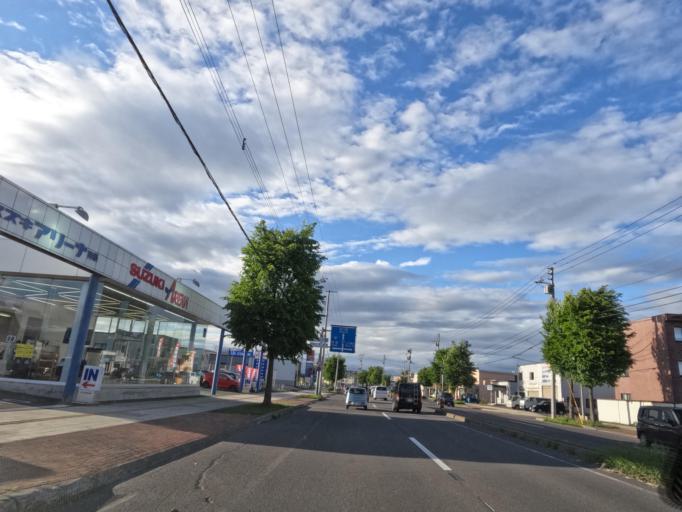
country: JP
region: Hokkaido
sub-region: Asahikawa-shi
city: Asahikawa
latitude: 43.7463
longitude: 142.3578
